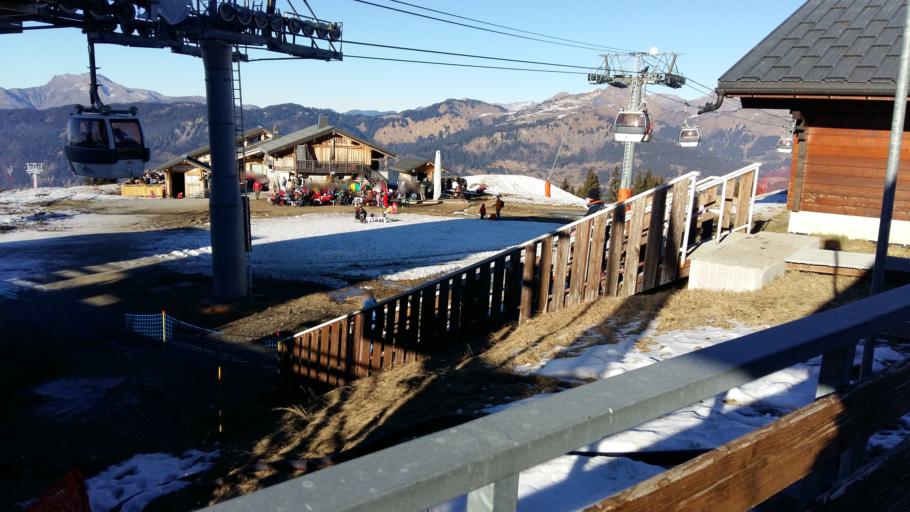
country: FR
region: Rhone-Alpes
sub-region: Departement de la Haute-Savoie
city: Samoens
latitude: 46.0554
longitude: 6.7025
